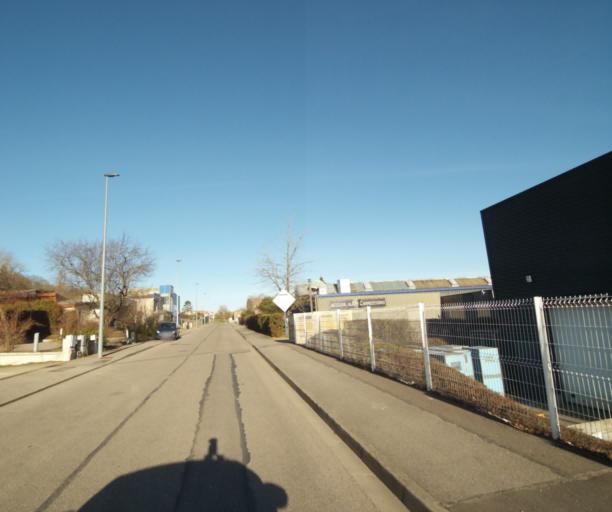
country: FR
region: Lorraine
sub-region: Departement de Meurthe-et-Moselle
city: Seichamps
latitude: 48.7147
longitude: 6.2514
